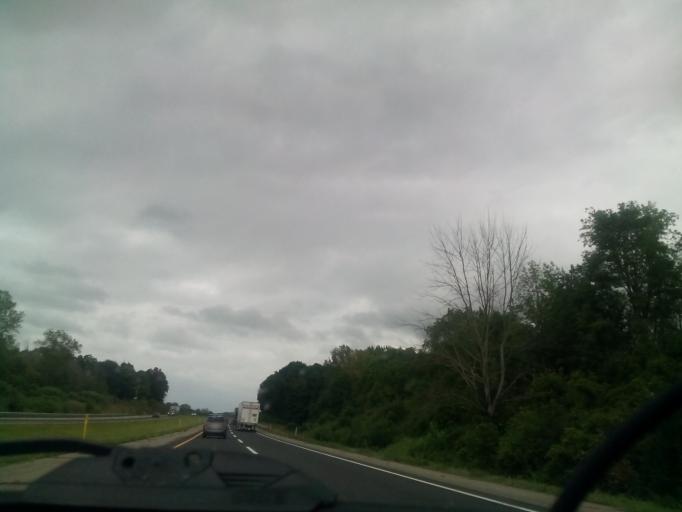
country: US
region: Indiana
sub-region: Steuben County
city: Hamilton
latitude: 41.6393
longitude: -84.8293
